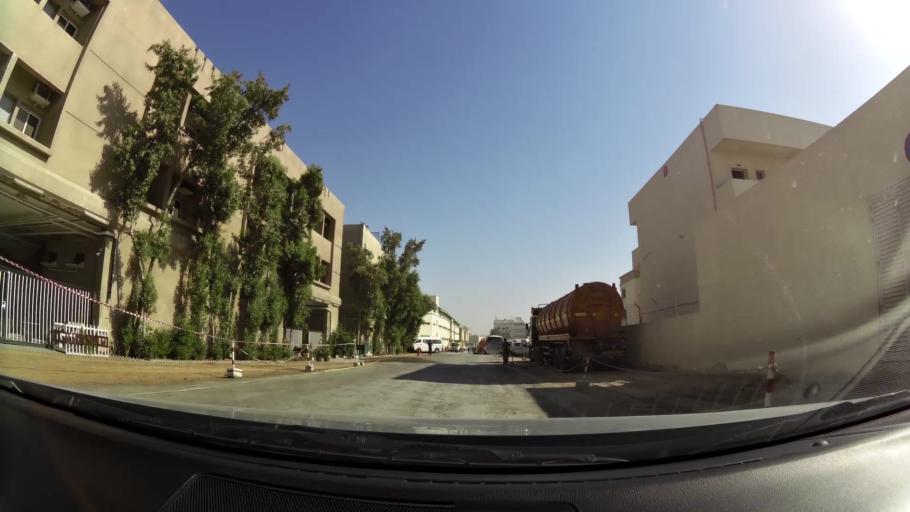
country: AE
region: Dubai
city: Dubai
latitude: 25.0074
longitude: 55.1044
